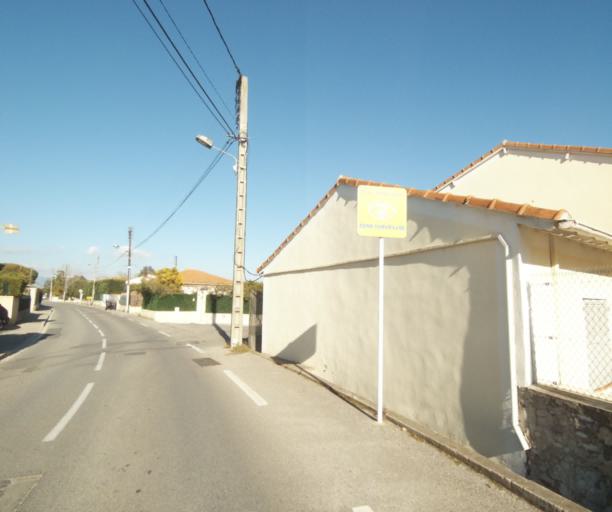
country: FR
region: Provence-Alpes-Cote d'Azur
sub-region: Departement des Alpes-Maritimes
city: Biot
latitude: 43.6043
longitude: 7.1173
